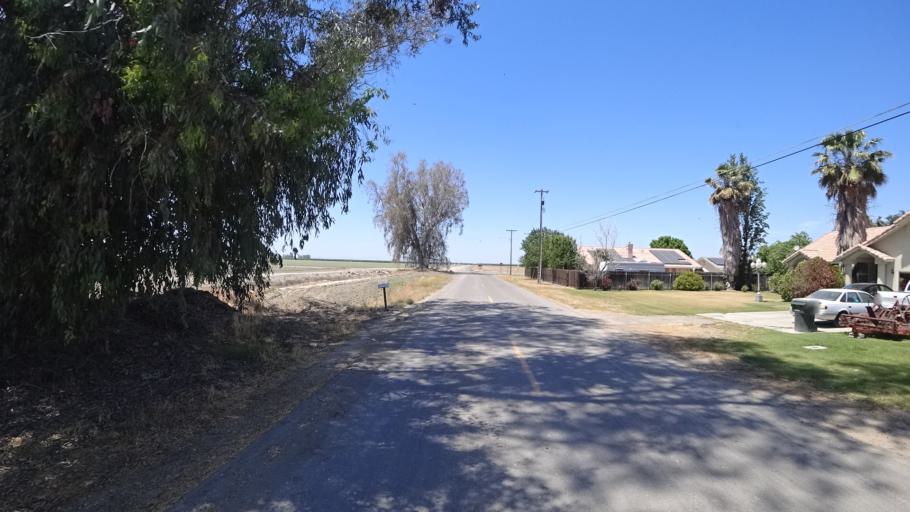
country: US
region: California
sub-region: Kings County
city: Corcoran
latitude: 36.1161
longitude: -119.5800
